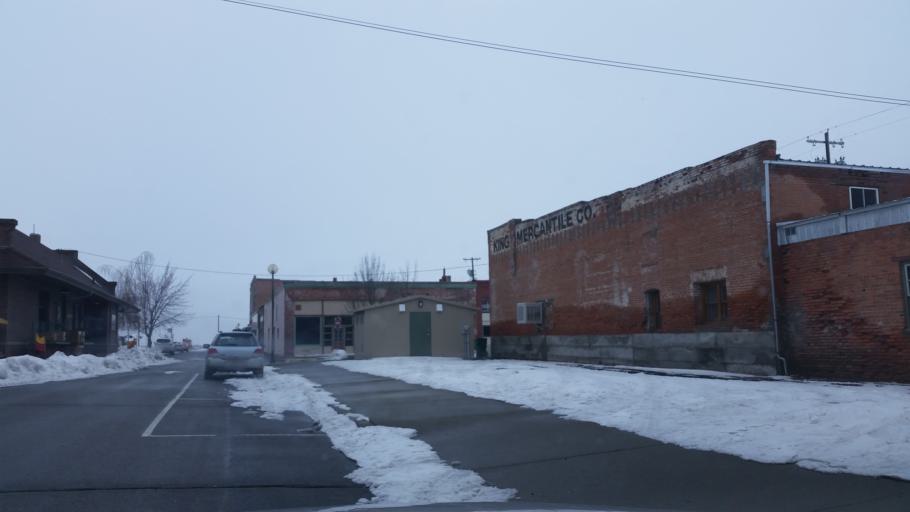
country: US
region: Washington
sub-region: Adams County
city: Ritzville
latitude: 47.1268
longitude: -118.3796
